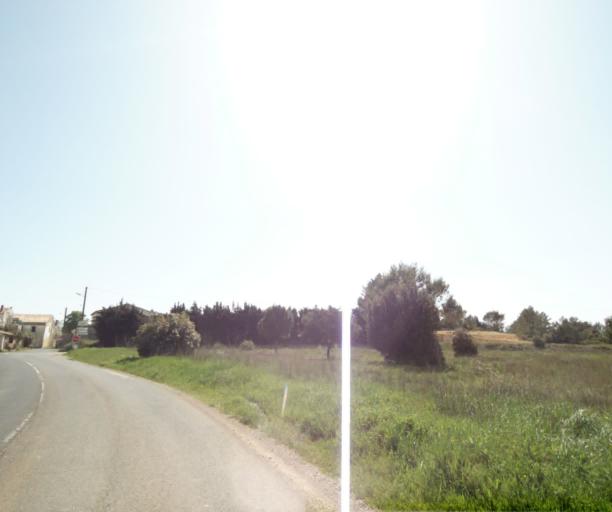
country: FR
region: Languedoc-Roussillon
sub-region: Departement de l'Herault
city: Murviel-les-Montpellier
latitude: 43.6396
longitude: 3.7496
